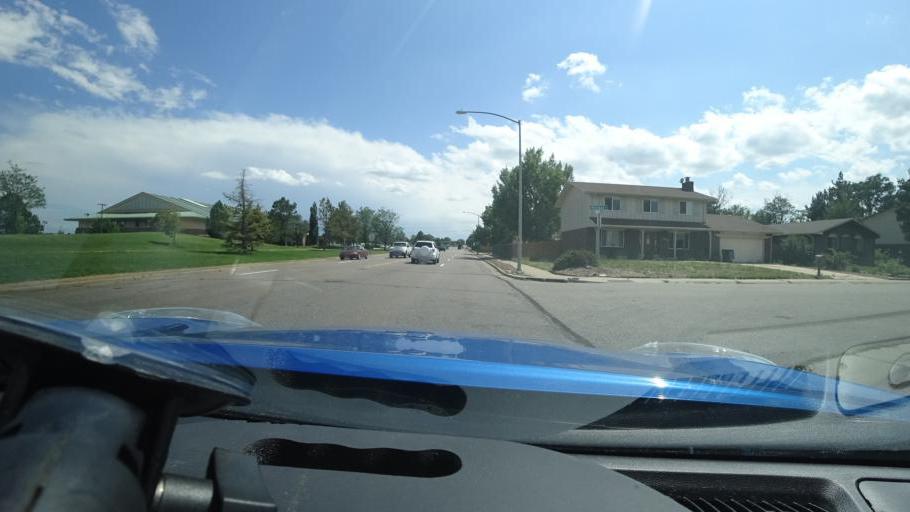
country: US
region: Colorado
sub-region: Adams County
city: Aurora
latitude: 39.6851
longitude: -104.8472
